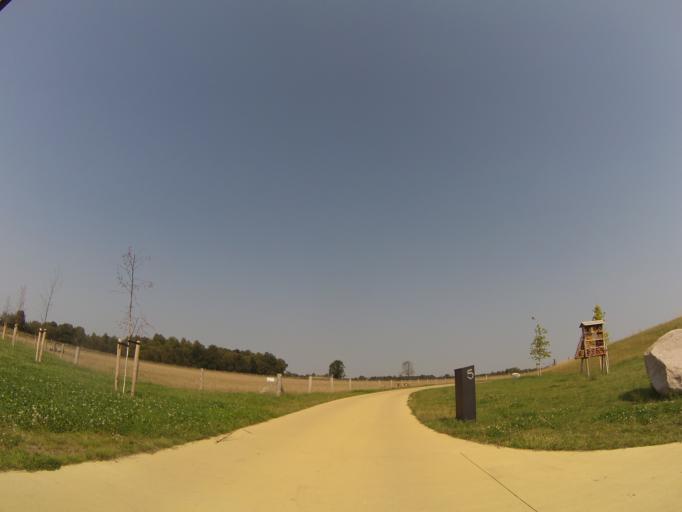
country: NL
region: Drenthe
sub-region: Gemeente Emmen
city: Klazienaveen
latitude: 52.6770
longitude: 6.9999
